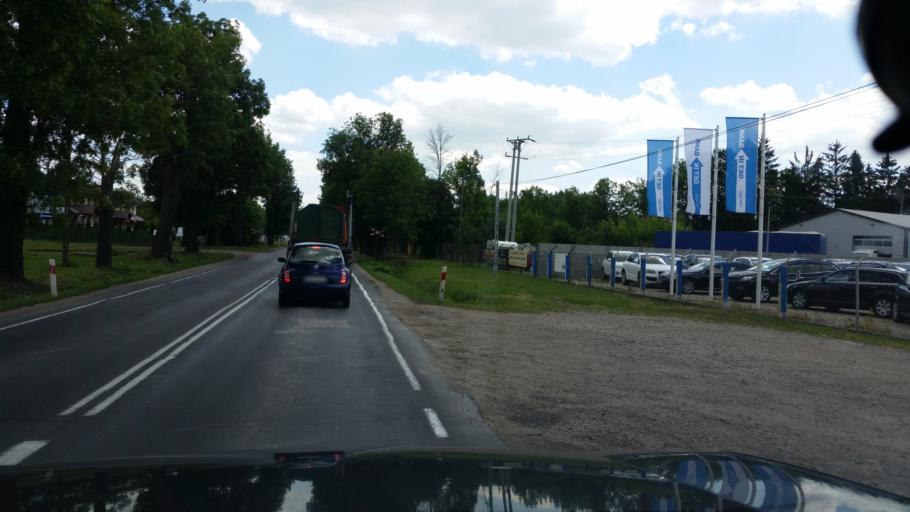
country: PL
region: Masovian Voivodeship
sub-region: Powiat ostrowski
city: Ostrow Mazowiecka
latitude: 52.8281
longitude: 21.8788
